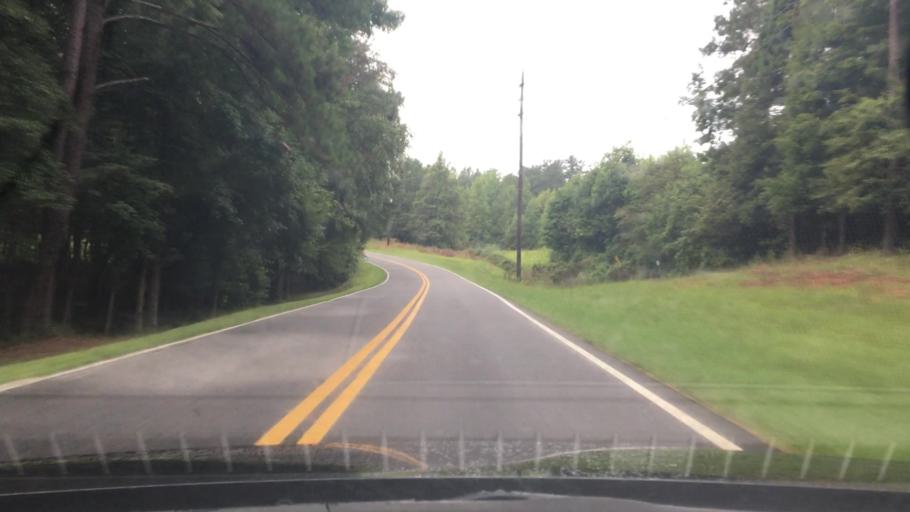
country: US
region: Georgia
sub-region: Spalding County
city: Experiment
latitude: 33.2578
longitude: -84.3886
